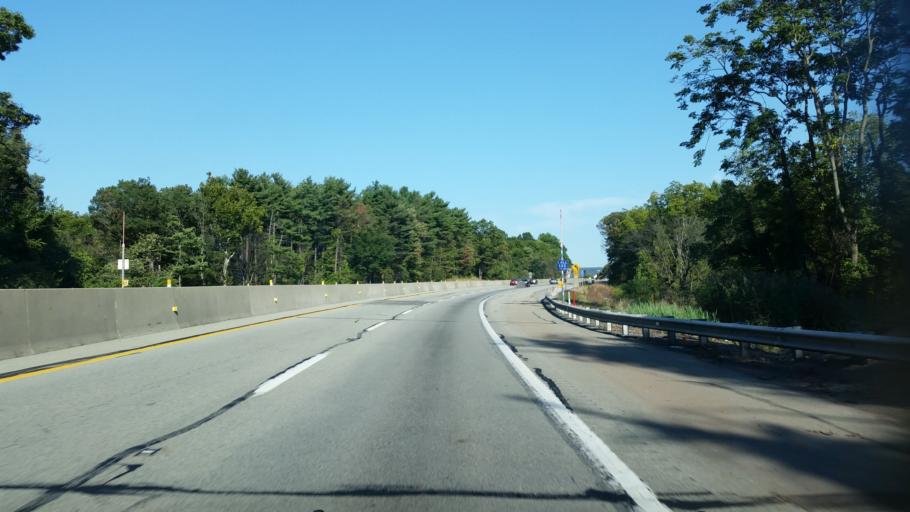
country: US
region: Pennsylvania
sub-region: Fulton County
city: McConnellsburg
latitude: 40.0436
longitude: -78.0356
